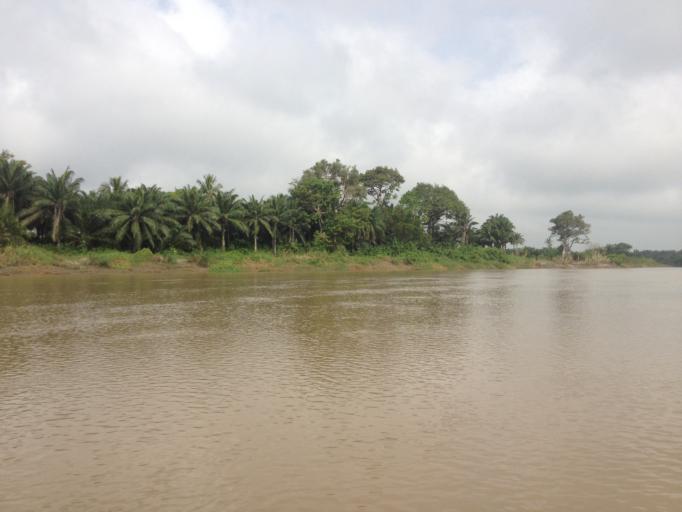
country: BJ
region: Mono
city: Come
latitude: 6.3884
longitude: 1.7734
